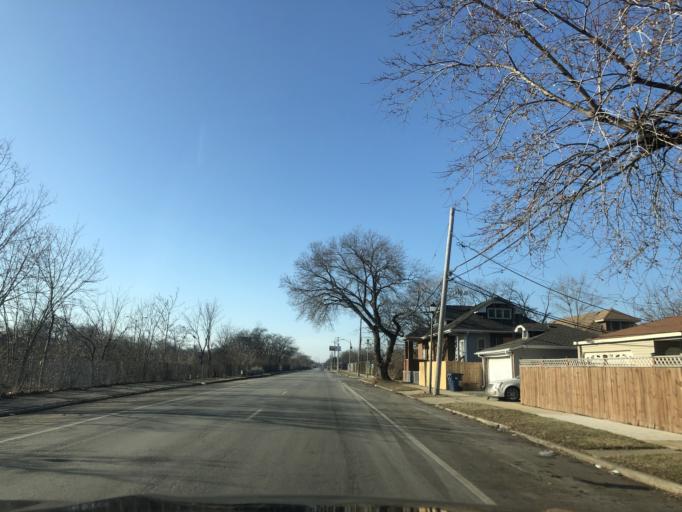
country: US
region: Illinois
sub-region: Cook County
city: Maywood
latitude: 41.8717
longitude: -87.8435
